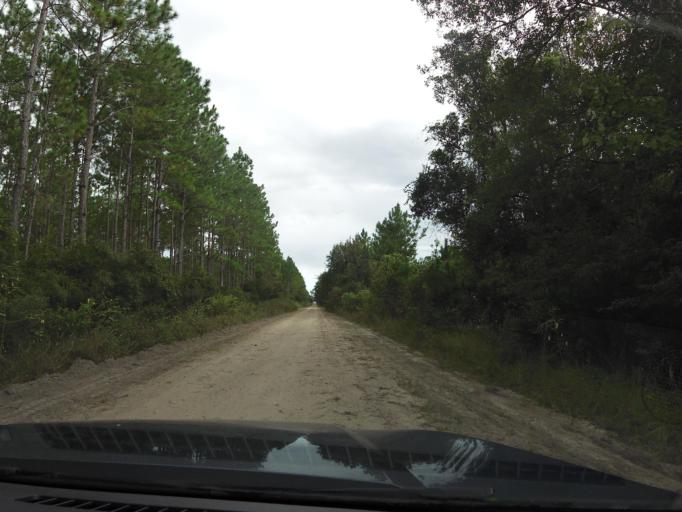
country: US
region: Florida
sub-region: Flagler County
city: Palm Coast
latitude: 29.5757
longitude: -81.3407
